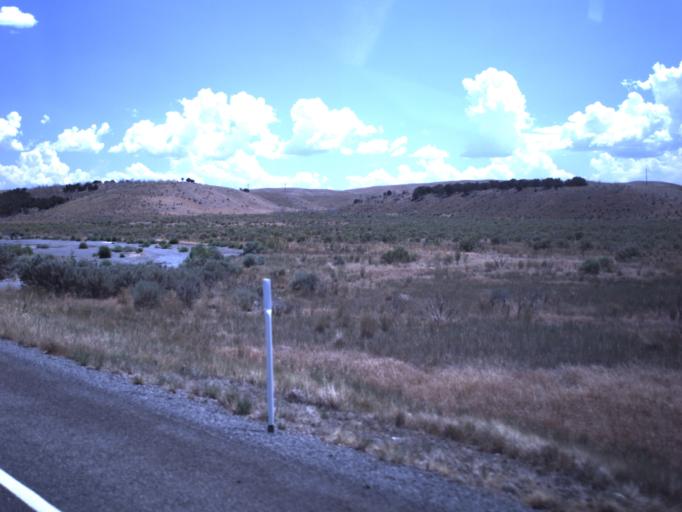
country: US
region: Utah
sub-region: Juab County
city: Nephi
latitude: 39.6324
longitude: -112.1130
